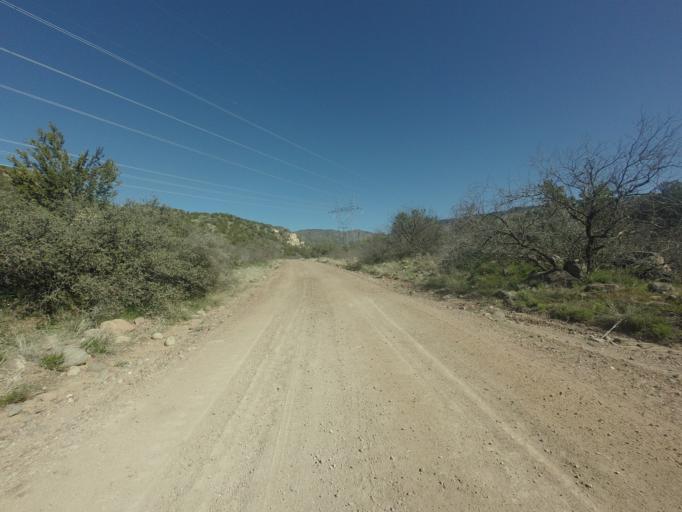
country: US
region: Arizona
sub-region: Gila County
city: Pine
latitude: 34.3926
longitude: -111.6505
